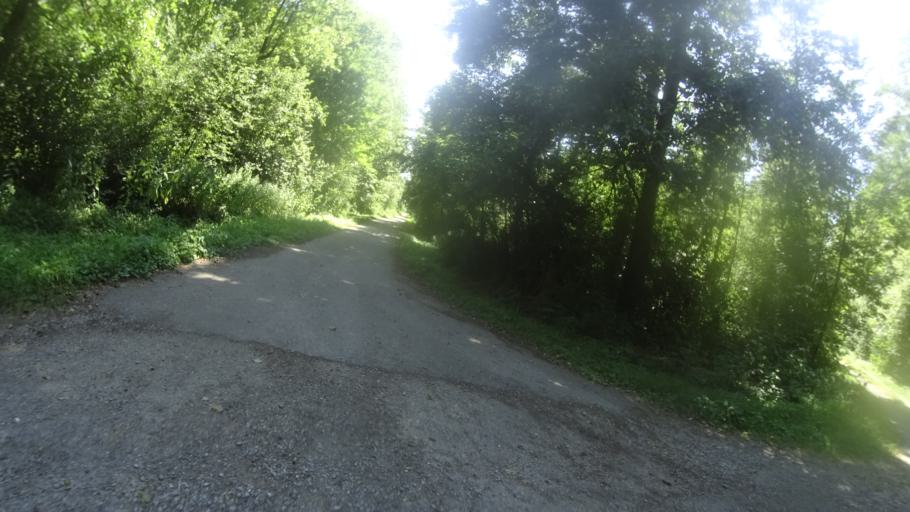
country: DE
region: Baden-Wuerttemberg
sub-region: Karlsruhe Region
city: Karlsruhe
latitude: 49.0133
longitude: 8.4563
